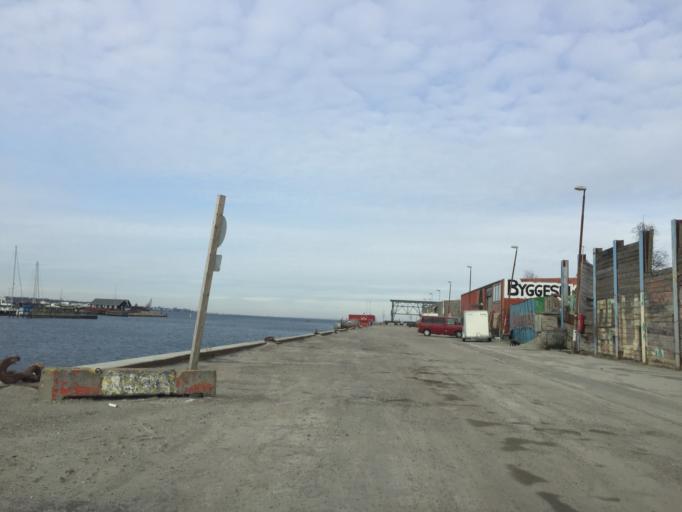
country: DK
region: Capital Region
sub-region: Gentofte Kommune
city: Charlottenlund
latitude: 55.7152
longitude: 12.5926
